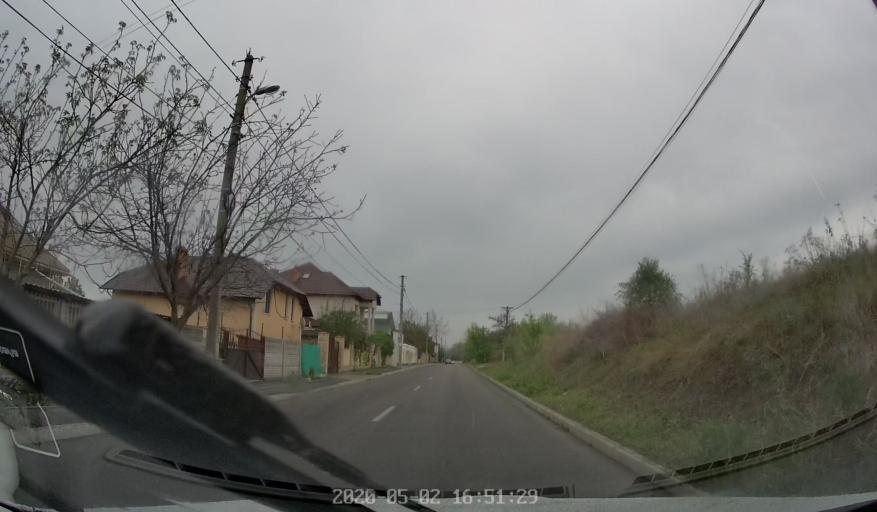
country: MD
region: Chisinau
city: Chisinau
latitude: 46.9625
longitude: 28.8314
